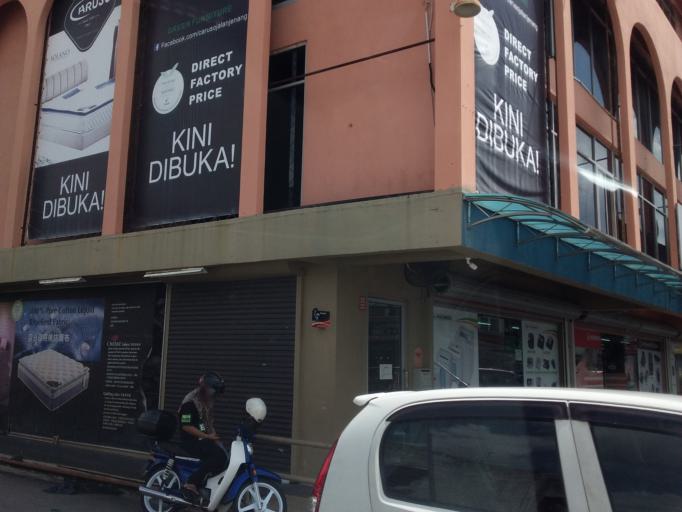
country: MY
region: Johor
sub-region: Daerah Batu Pahat
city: Batu Pahat
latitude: 1.8540
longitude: 102.9277
